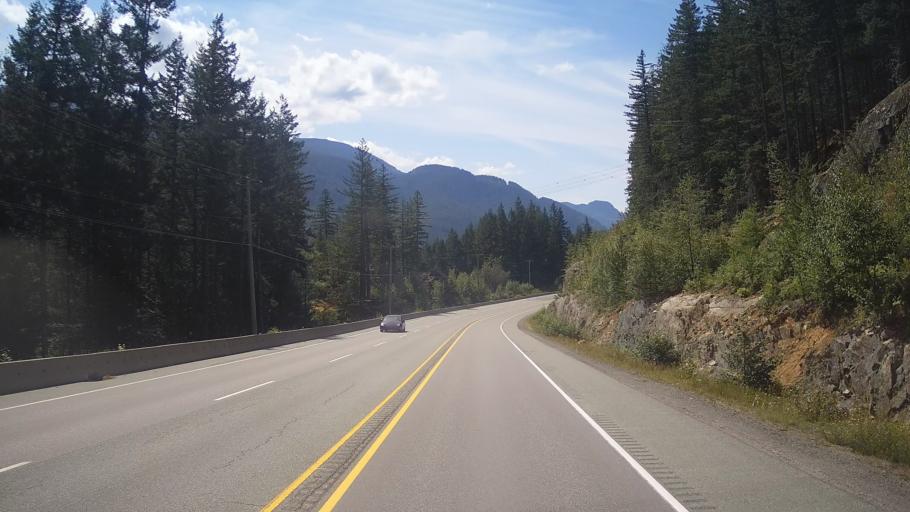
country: CA
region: British Columbia
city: Whistler
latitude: 50.0265
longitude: -123.1209
